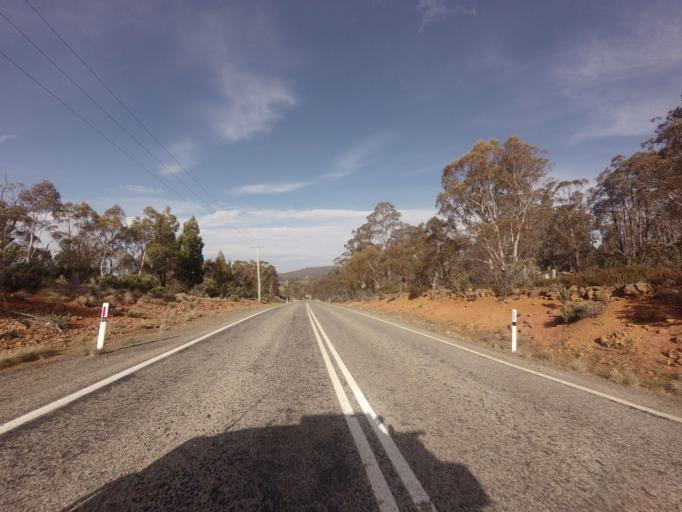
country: AU
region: Tasmania
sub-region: Meander Valley
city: Deloraine
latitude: -41.9914
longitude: 146.6994
